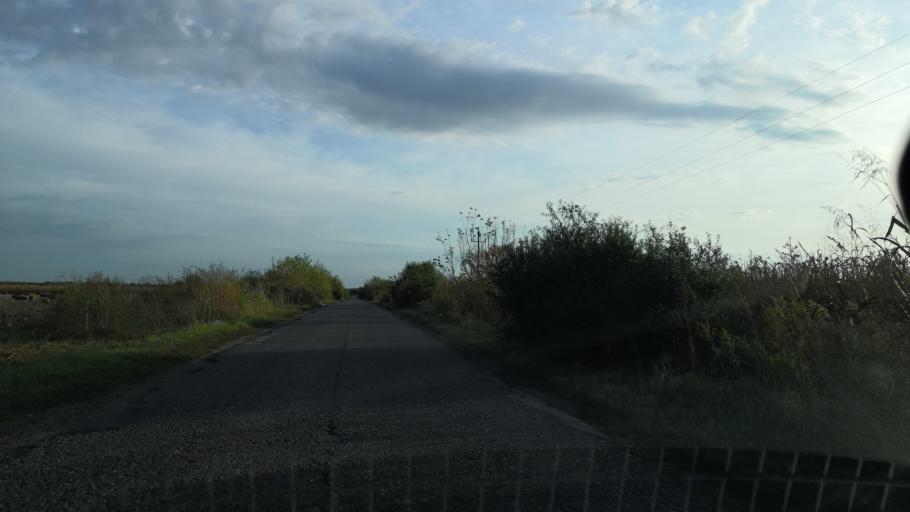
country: RS
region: Autonomna Pokrajina Vojvodina
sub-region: Sremski Okrug
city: Stara Pazova
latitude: 45.0040
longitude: 20.1658
